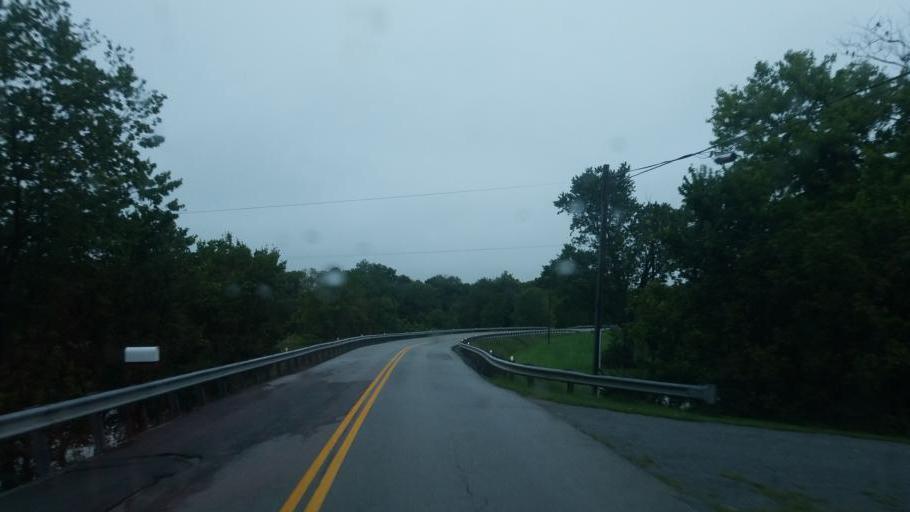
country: US
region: Kentucky
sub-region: Fleming County
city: Flemingsburg
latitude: 38.4148
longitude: -83.6934
